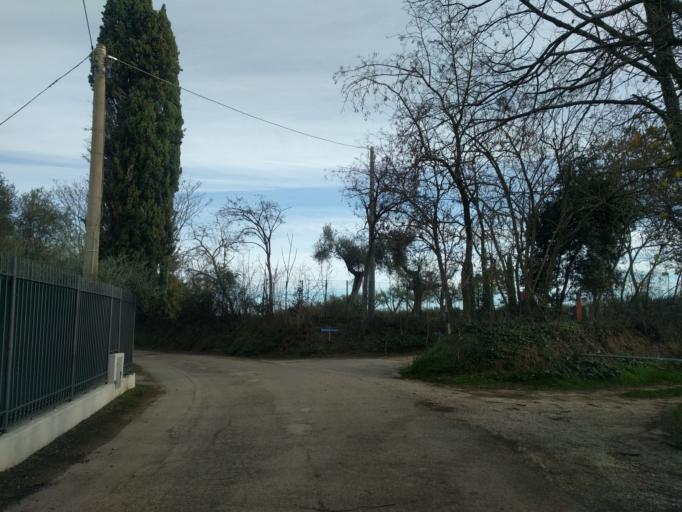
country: IT
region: The Marches
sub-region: Provincia di Pesaro e Urbino
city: Centinarola
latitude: 43.8251
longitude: 12.9848
